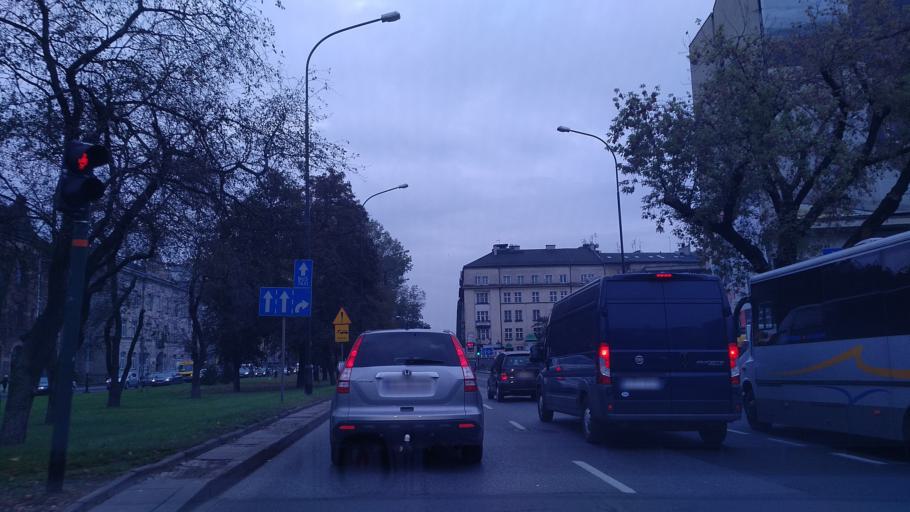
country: PL
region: Lesser Poland Voivodeship
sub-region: Krakow
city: Krakow
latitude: 50.0591
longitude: 19.9250
